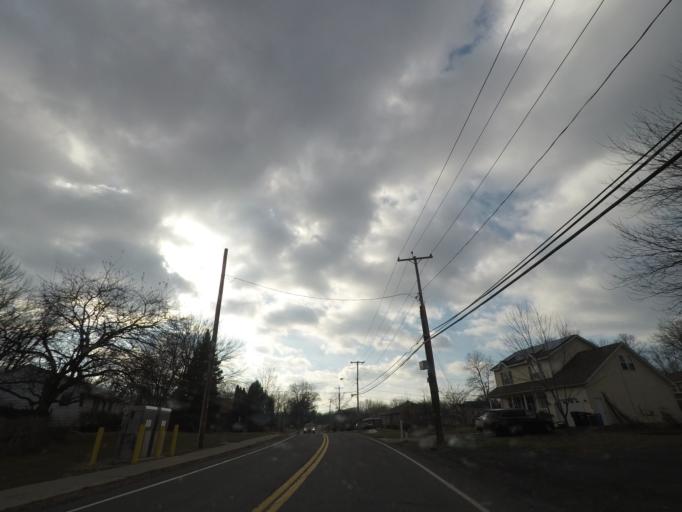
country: US
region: New York
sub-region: Albany County
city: McKownville
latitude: 42.6676
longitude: -73.8287
